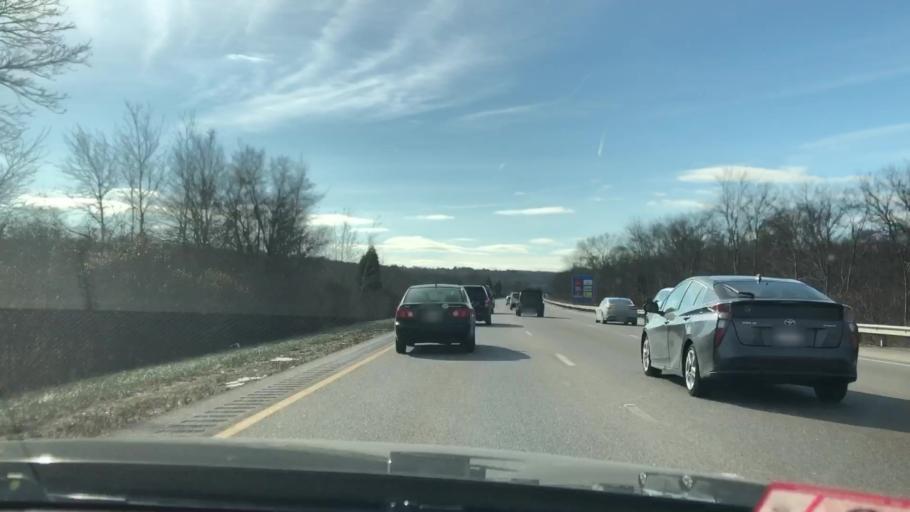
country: US
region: Massachusetts
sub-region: Norfolk County
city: Canton
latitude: 42.1613
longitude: -71.1804
